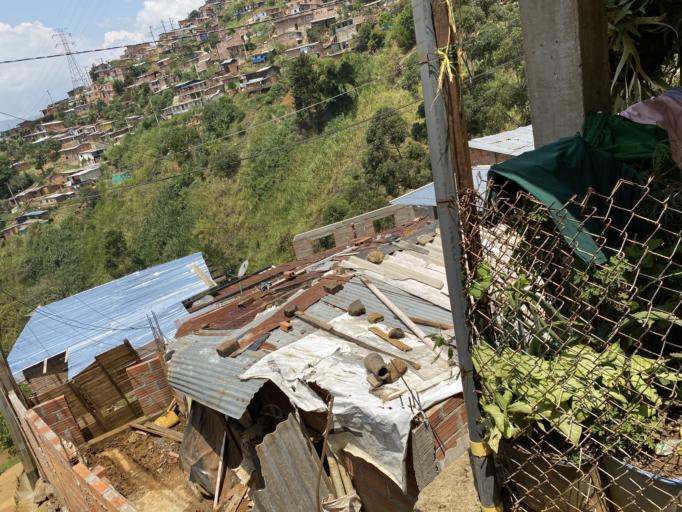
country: CO
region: Antioquia
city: Medellin
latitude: 6.2670
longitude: -75.5406
